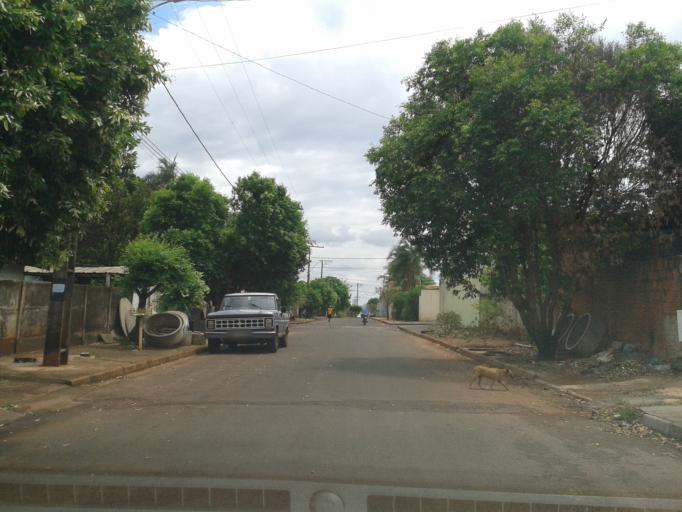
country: BR
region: Minas Gerais
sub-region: Ituiutaba
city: Ituiutaba
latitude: -18.9927
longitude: -49.4639
